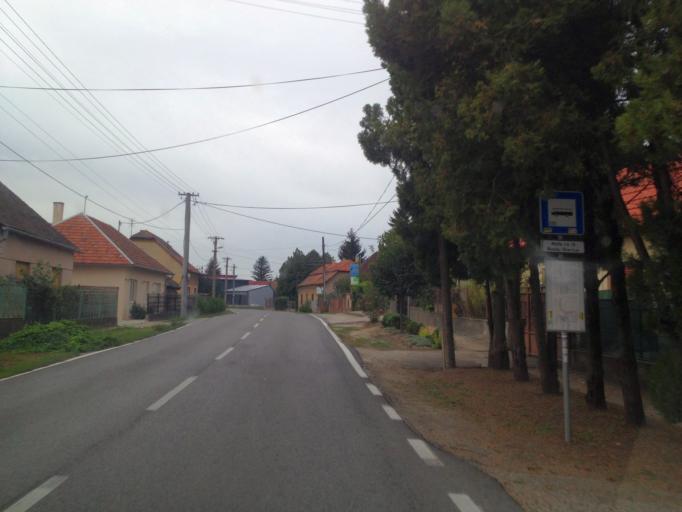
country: HU
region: Komarom-Esztergom
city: Nyergesujfalu
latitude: 47.7906
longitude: 18.6084
